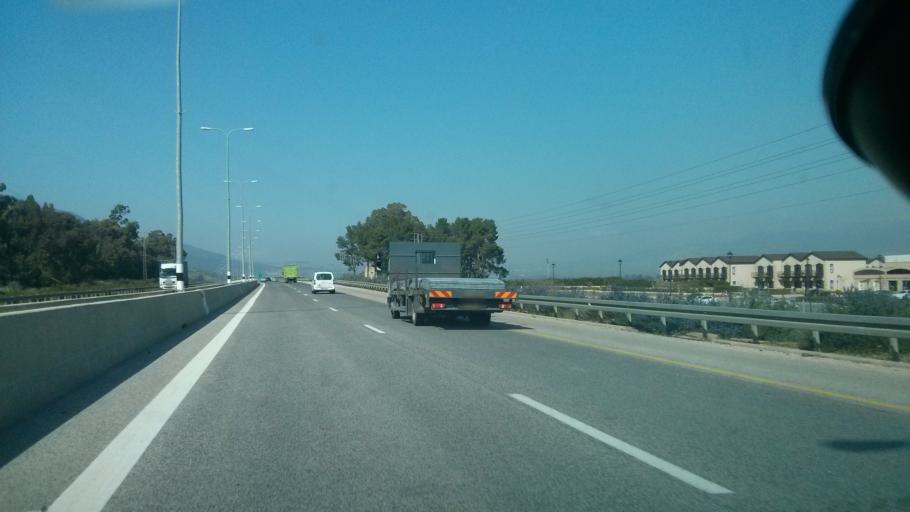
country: IL
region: Northern District
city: Qiryat Shemona
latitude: 33.1167
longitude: 35.5719
